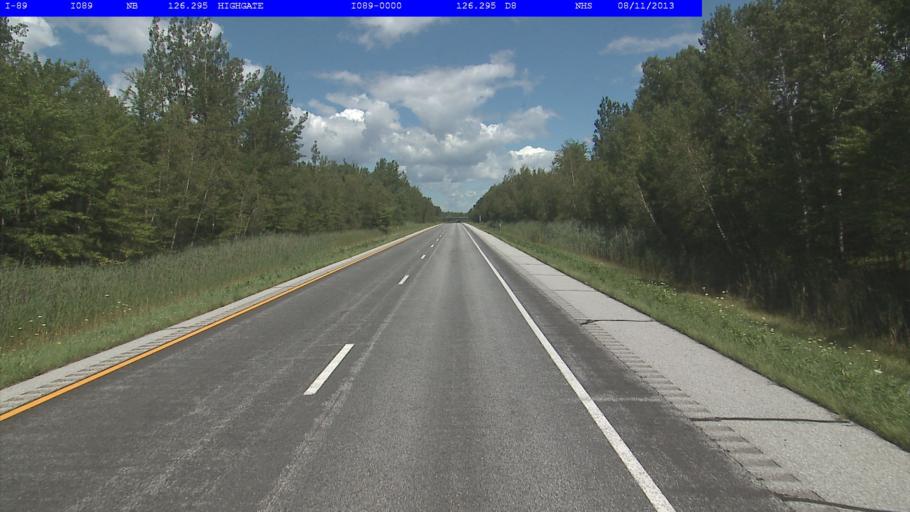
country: US
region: Vermont
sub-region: Franklin County
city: Swanton
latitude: 44.9632
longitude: -73.1067
